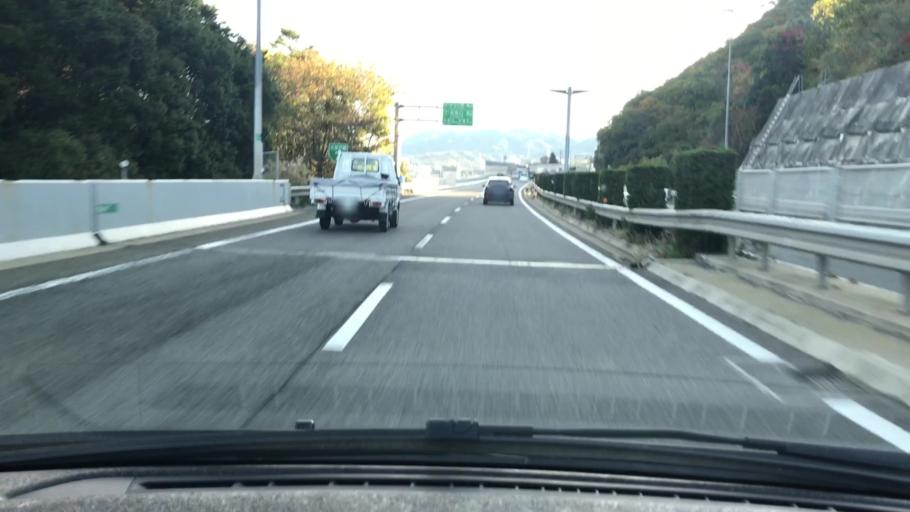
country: JP
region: Hyogo
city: Kobe
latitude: 34.7589
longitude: 135.1615
